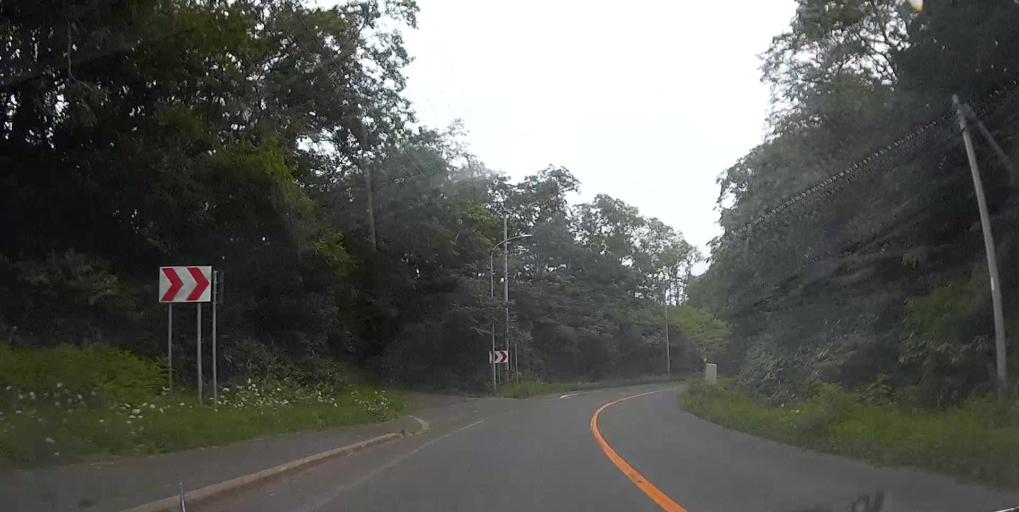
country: JP
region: Hokkaido
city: Iwanai
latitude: 42.4362
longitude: 139.9934
